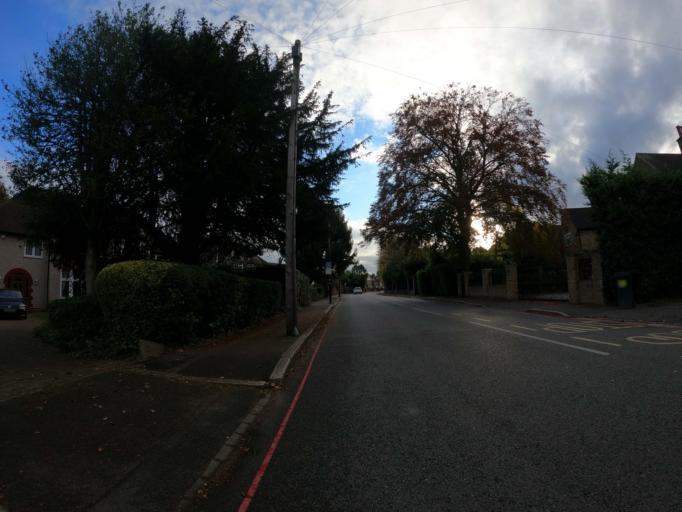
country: GB
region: England
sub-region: Greater London
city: Isleworth
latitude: 51.4870
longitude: -0.3414
